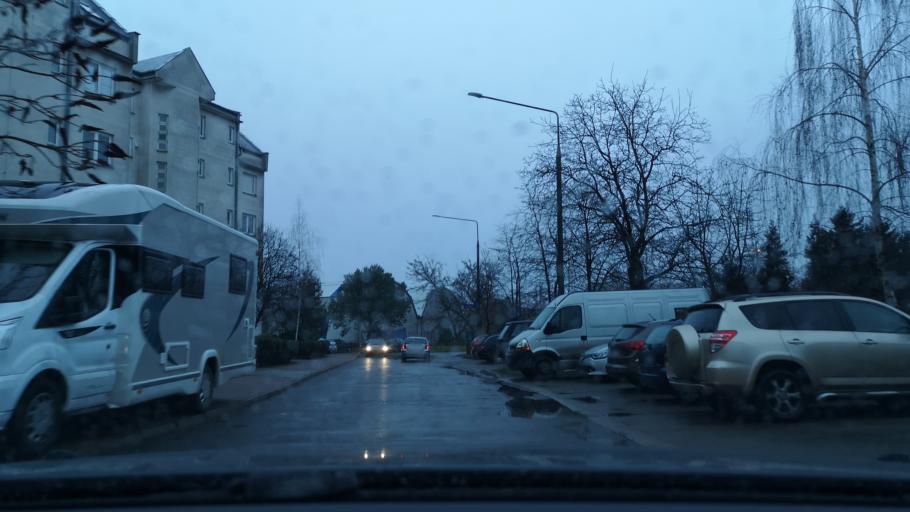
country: PL
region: Masovian Voivodeship
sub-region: Warszawa
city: Bemowo
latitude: 52.2450
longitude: 20.9174
